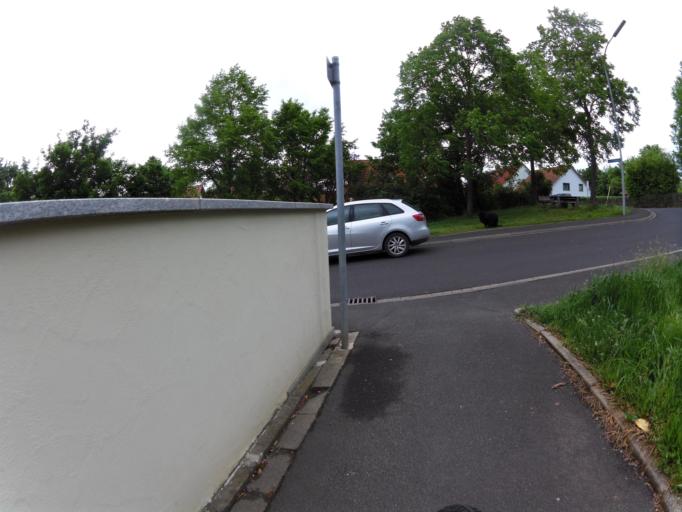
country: DE
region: Bavaria
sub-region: Regierungsbezirk Unterfranken
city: Volkach
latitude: 49.8651
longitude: 10.2413
